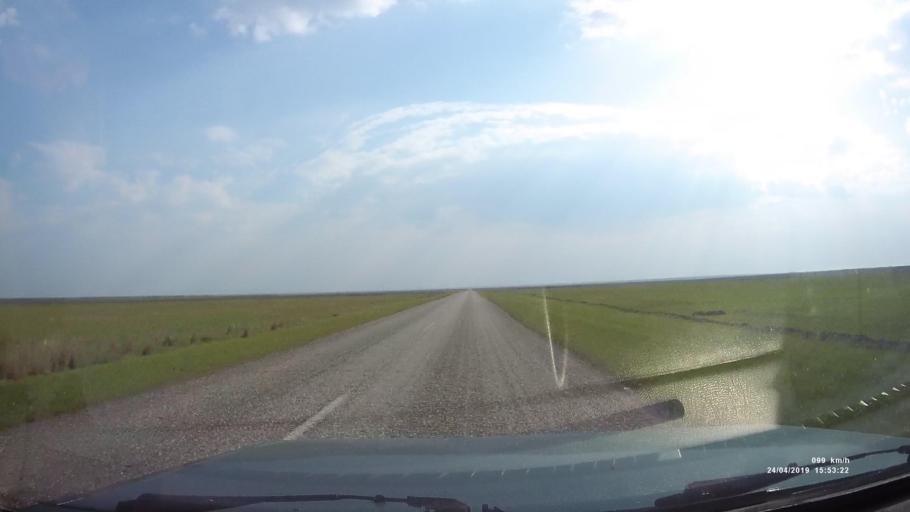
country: RU
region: Kalmykiya
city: Yashalta
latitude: 46.5991
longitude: 42.5765
